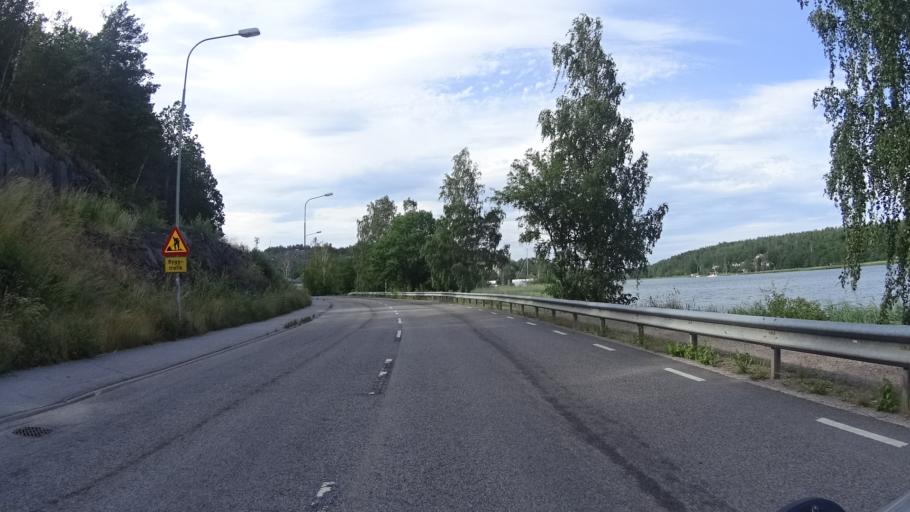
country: SE
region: Kalmar
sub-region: Vasterviks Kommun
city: Gamleby
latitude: 57.8942
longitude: 16.4152
